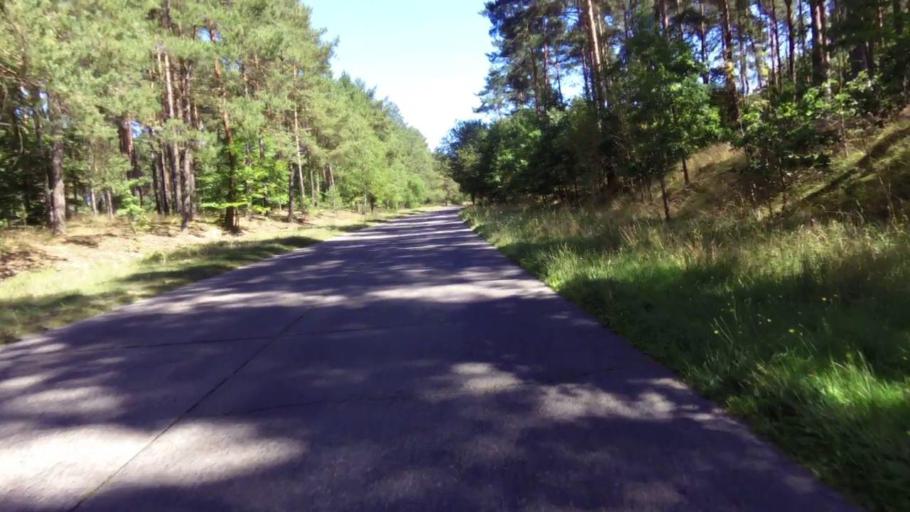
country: PL
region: West Pomeranian Voivodeship
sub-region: Powiat szczecinecki
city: Lubowo
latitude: 53.5872
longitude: 16.4600
